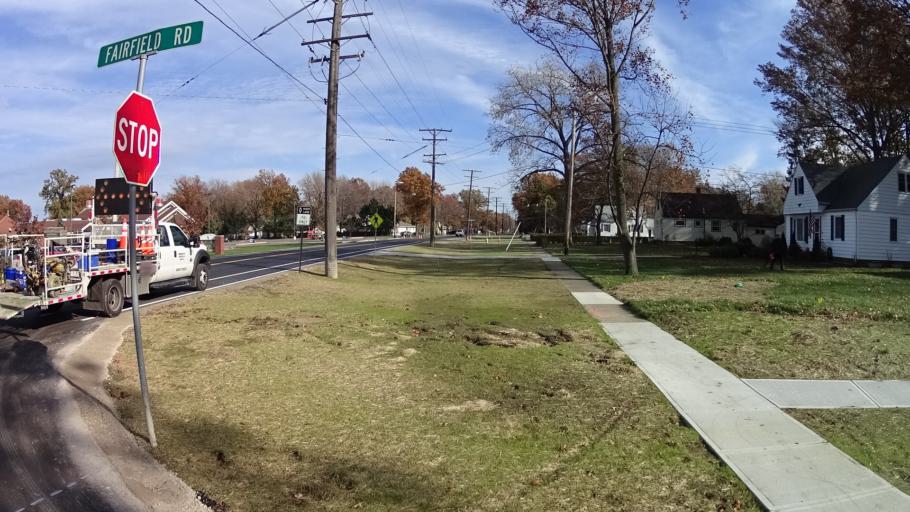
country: US
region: Ohio
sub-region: Lorain County
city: Avon Lake
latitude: 41.5093
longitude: -82.0267
